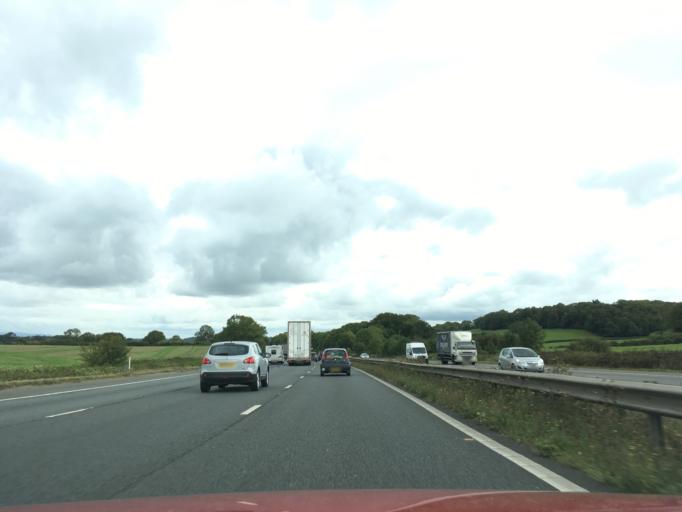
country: GB
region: England
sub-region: South Gloucestershire
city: Tytherington
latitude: 51.6093
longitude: -2.4675
